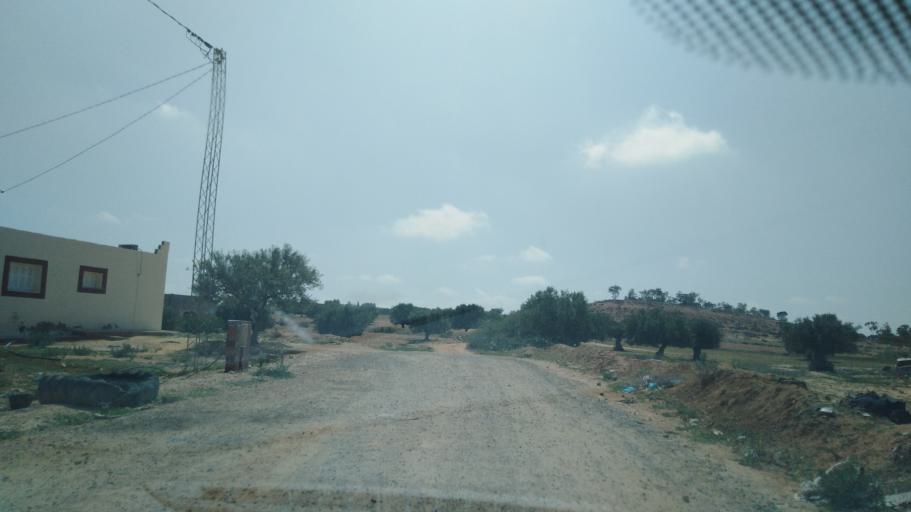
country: TN
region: Safaqis
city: Sfax
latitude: 34.7284
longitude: 10.5687
